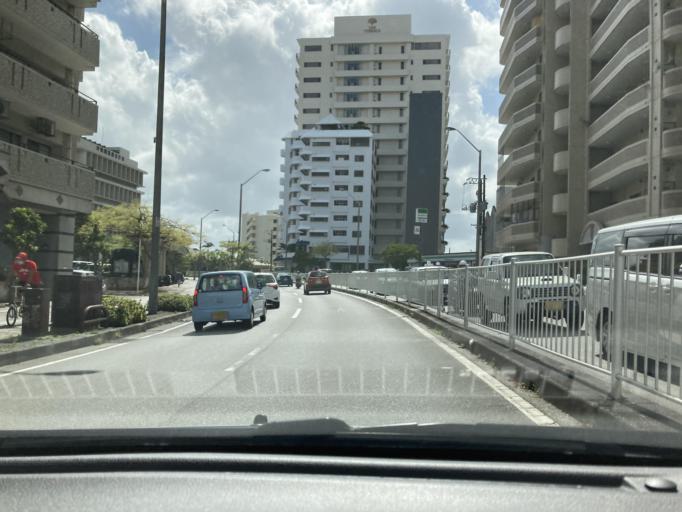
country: JP
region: Okinawa
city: Naha-shi
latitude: 26.2255
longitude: 127.6932
